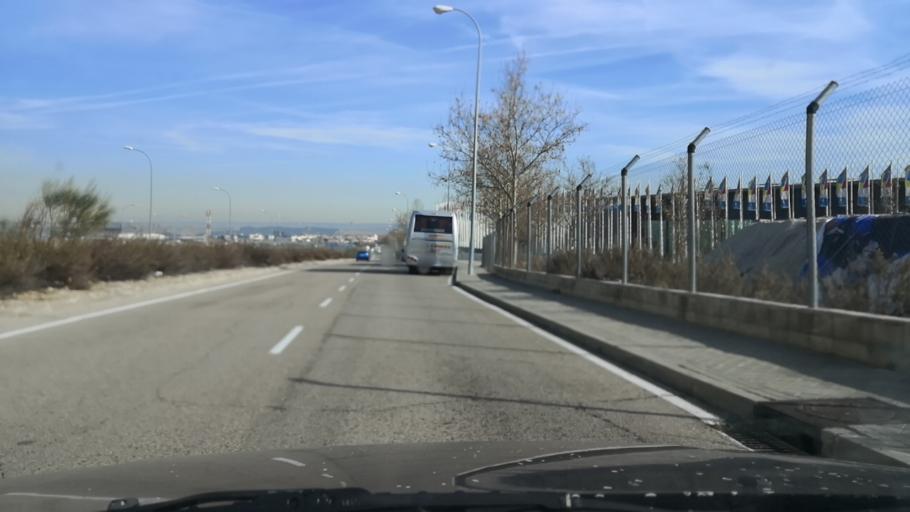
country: ES
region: Madrid
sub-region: Provincia de Madrid
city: Hortaleza
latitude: 40.4719
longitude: -3.6195
